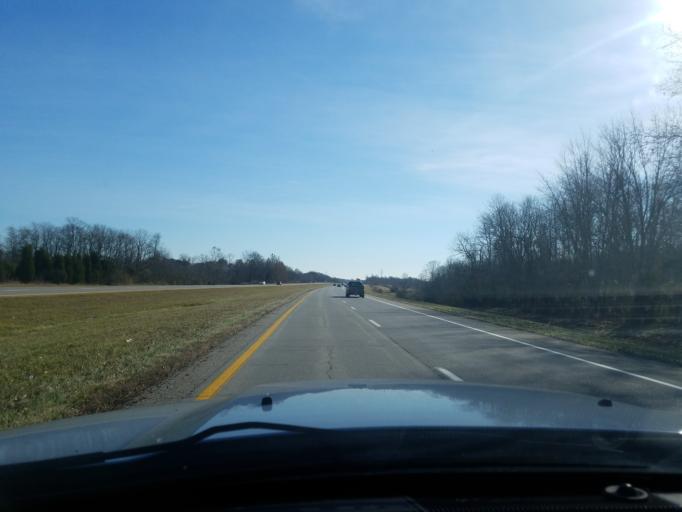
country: US
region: Ohio
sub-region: Brown County
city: Mount Orab
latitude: 39.0298
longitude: -83.8862
